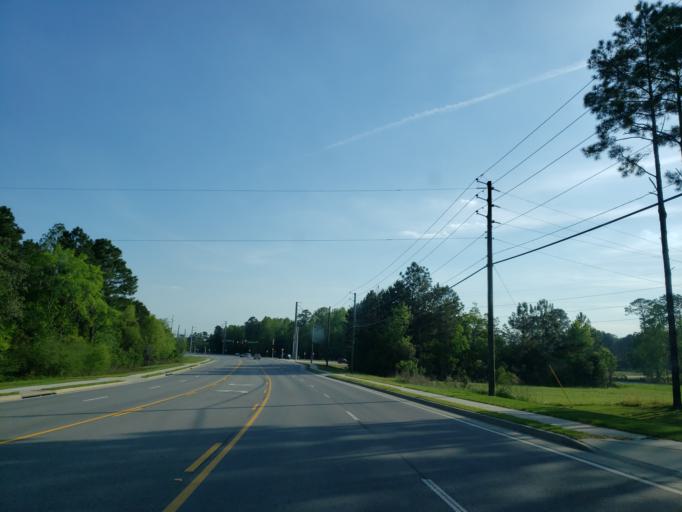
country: US
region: Georgia
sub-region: Tift County
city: Tifton
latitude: 31.4702
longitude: -83.5457
